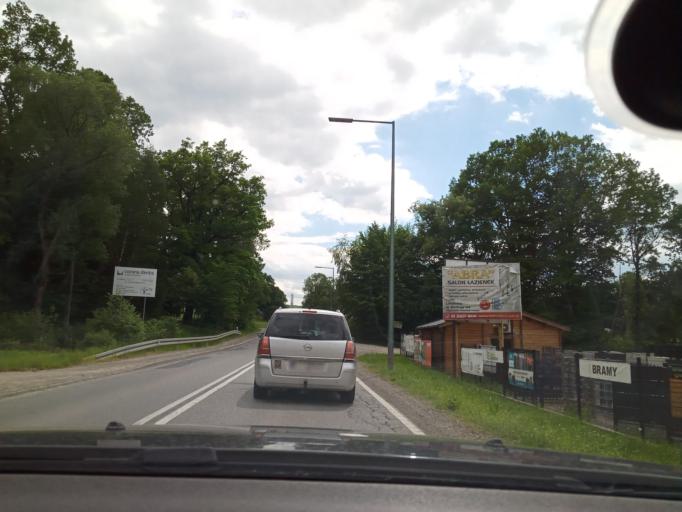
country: PL
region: Lesser Poland Voivodeship
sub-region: Powiat limanowski
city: Limanowa
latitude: 49.7343
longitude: 20.4005
